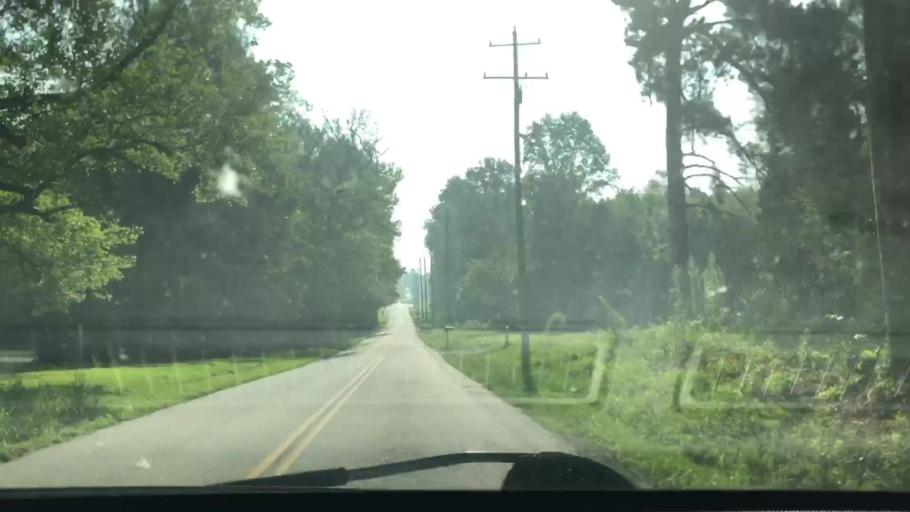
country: US
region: Arkansas
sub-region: Saline County
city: Bryant
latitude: 34.5957
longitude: -92.5195
